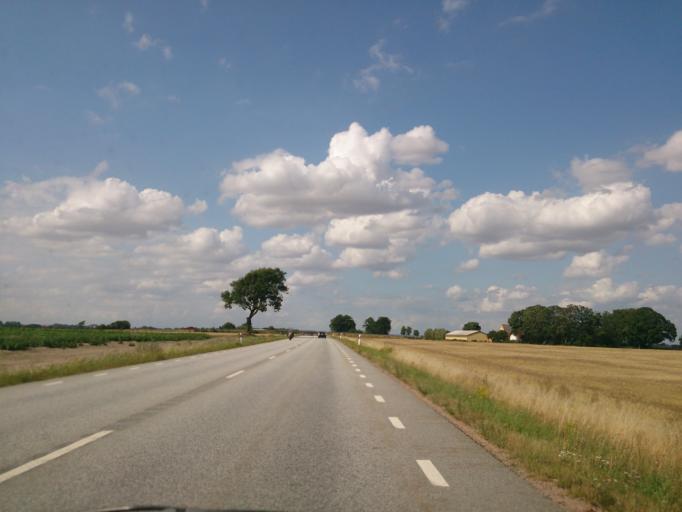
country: SE
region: Skane
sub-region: Kavlinge Kommun
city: Kaevlinge
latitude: 55.7805
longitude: 13.1339
